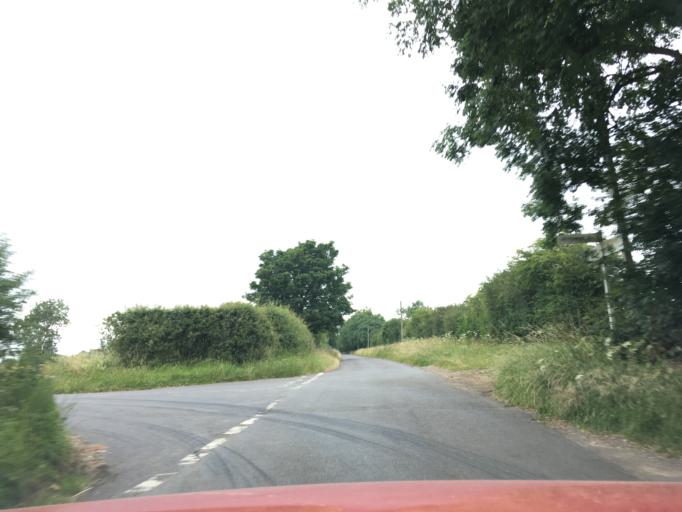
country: GB
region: England
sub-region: Oxfordshire
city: Hook Norton
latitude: 51.9388
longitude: -1.4495
